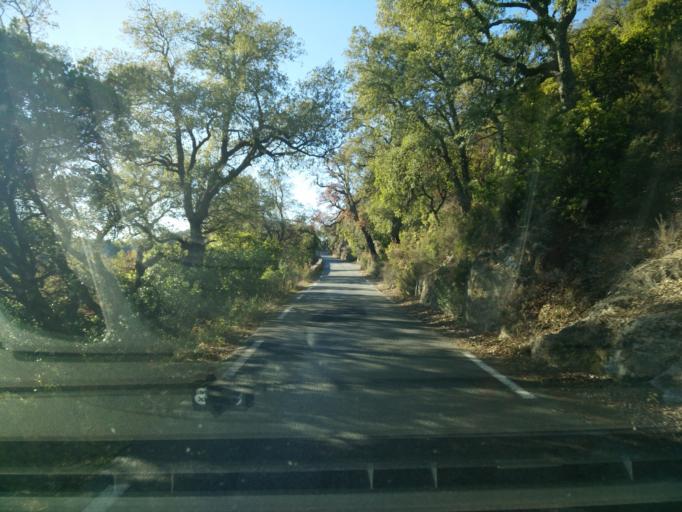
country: FR
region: Provence-Alpes-Cote d'Azur
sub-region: Departement du Var
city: Collobrieres
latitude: 43.2486
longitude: 6.3828
